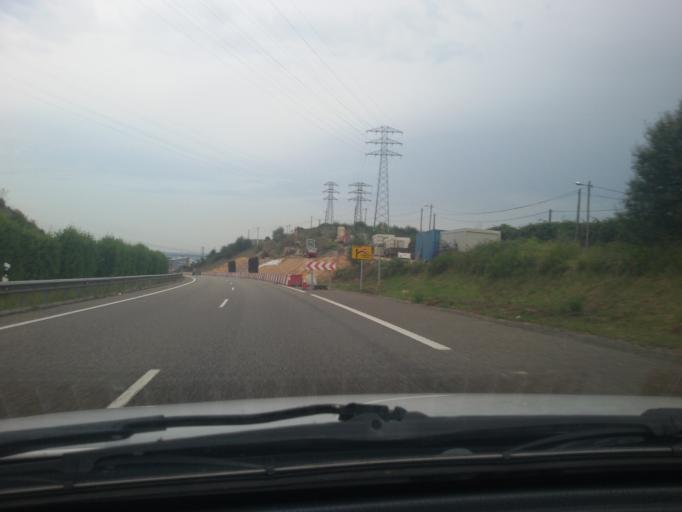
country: ES
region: Asturias
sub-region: Province of Asturias
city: Oviedo
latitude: 43.3810
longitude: -5.8337
